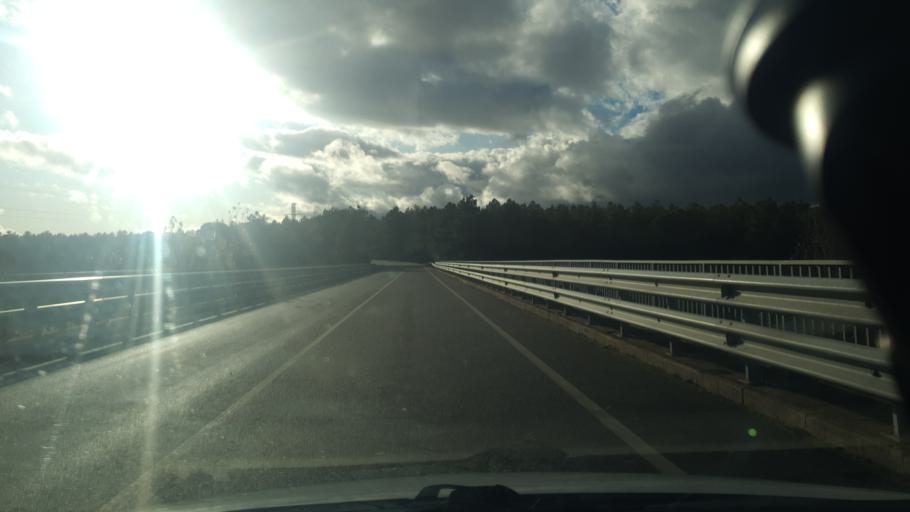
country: ES
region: Castille and Leon
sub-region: Provincia de Segovia
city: Santiuste de San Juan Bautista
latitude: 41.1522
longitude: -4.5361
